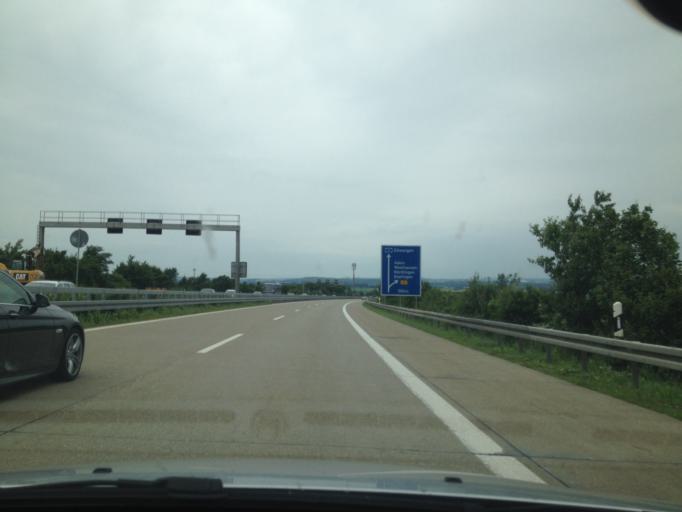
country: DE
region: Baden-Wuerttemberg
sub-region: Regierungsbezirk Stuttgart
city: Westhausen
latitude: 48.8787
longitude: 10.1654
